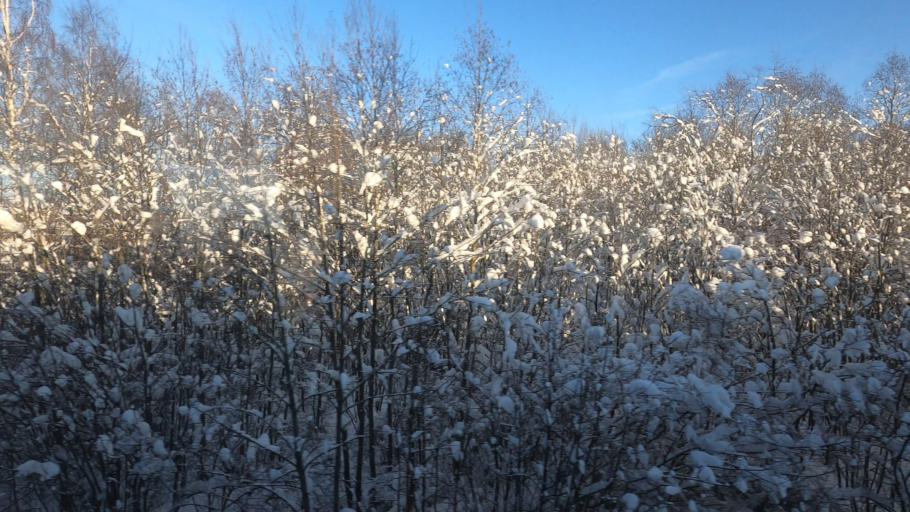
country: RU
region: Moskovskaya
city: Taldom
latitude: 56.7152
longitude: 37.5377
